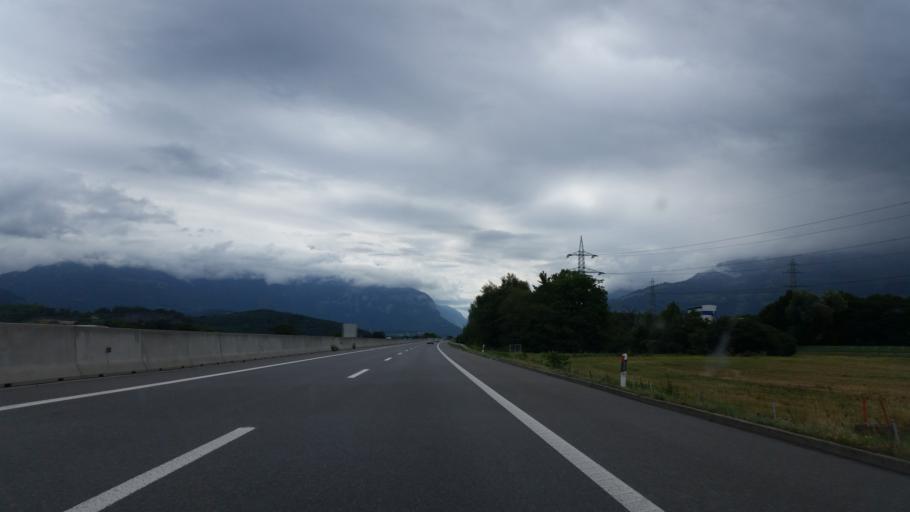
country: CH
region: Vaud
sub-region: Aigle District
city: Aigle
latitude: 46.3068
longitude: 6.9512
